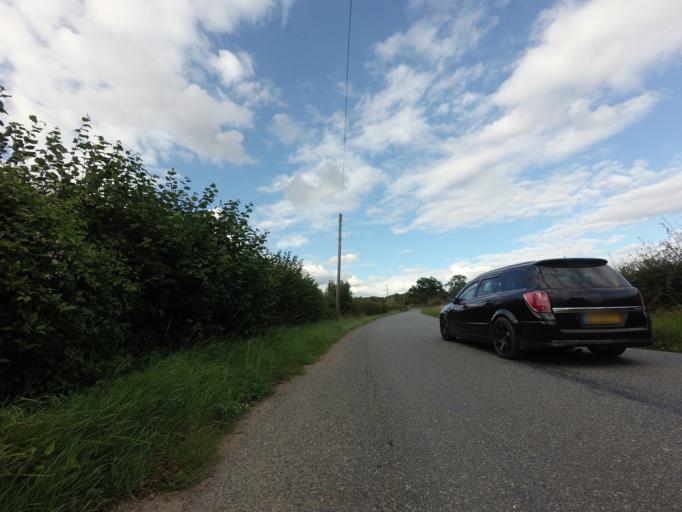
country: GB
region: England
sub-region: Kent
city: Marden
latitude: 51.2116
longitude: 0.5081
